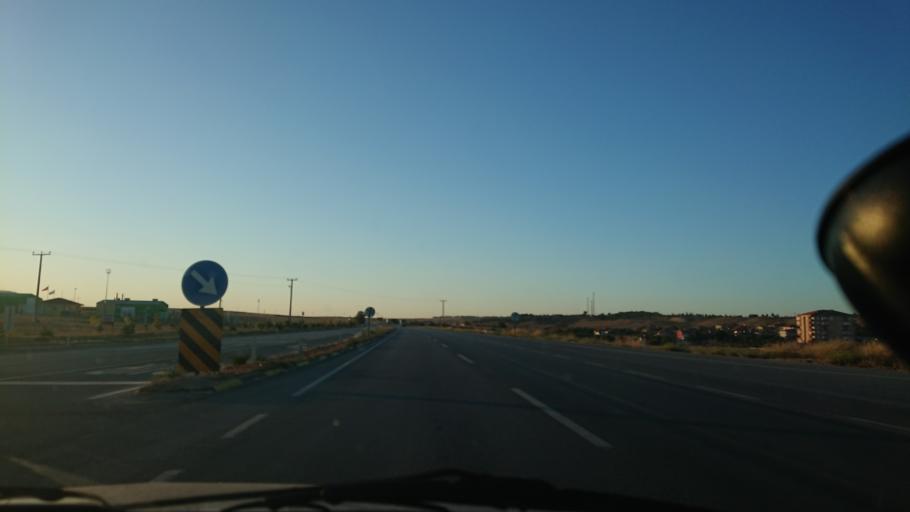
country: TR
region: Eskisehir
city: Mahmudiye
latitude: 39.4882
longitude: 30.9823
